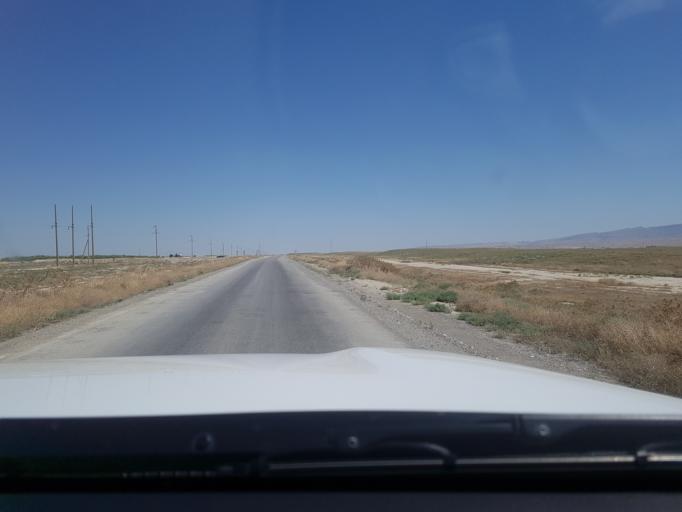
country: IR
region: Razavi Khorasan
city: Kalat-e Naderi
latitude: 37.0711
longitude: 60.1439
